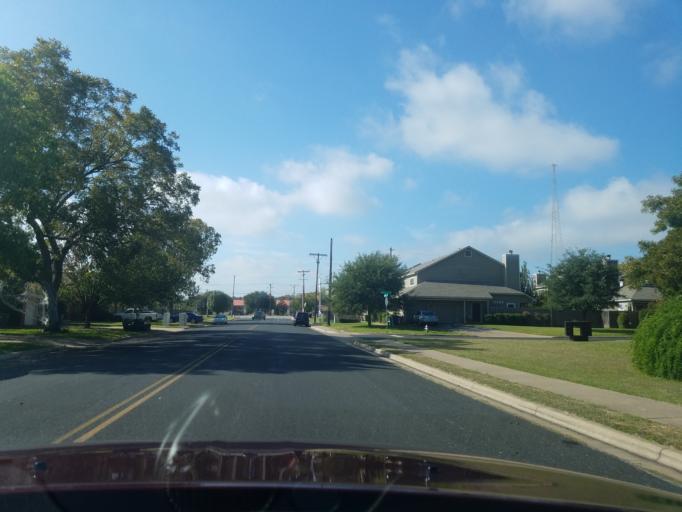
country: US
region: Texas
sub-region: Williamson County
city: Jollyville
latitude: 30.4460
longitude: -97.7769
